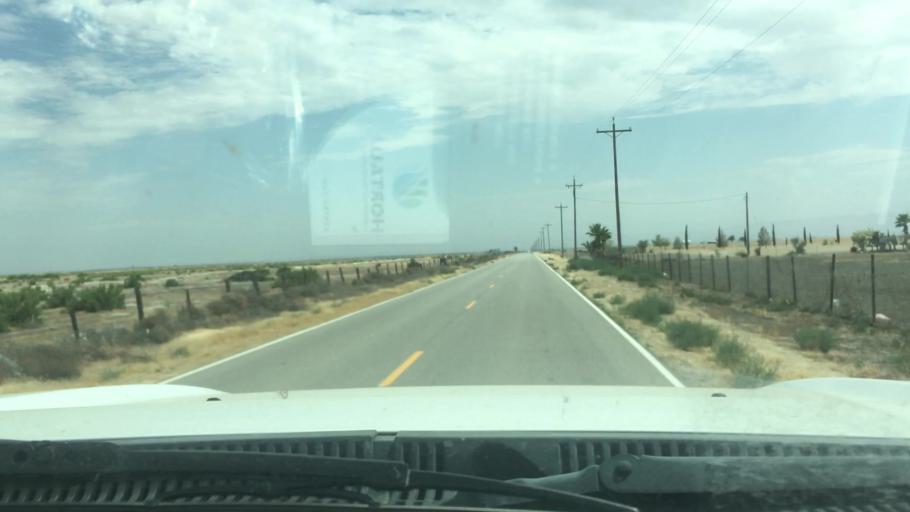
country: US
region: California
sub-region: Kern County
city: Lost Hills
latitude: 35.7003
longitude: -119.5797
